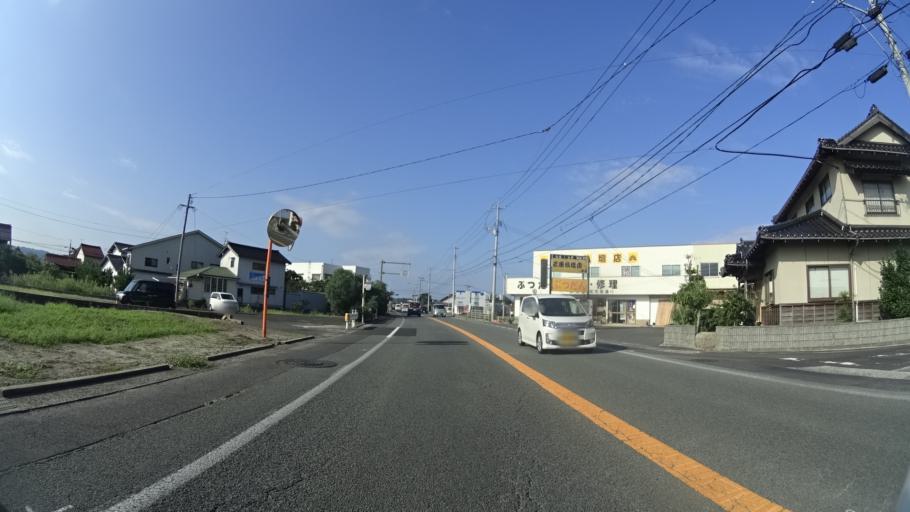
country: JP
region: Shimane
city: Izumo
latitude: 35.3335
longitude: 132.6803
